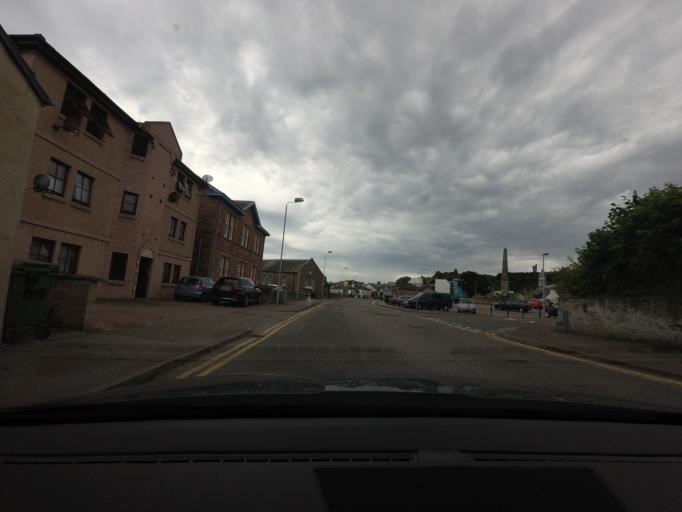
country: GB
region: Scotland
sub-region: Highland
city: Dingwall
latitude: 57.5982
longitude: -4.4287
